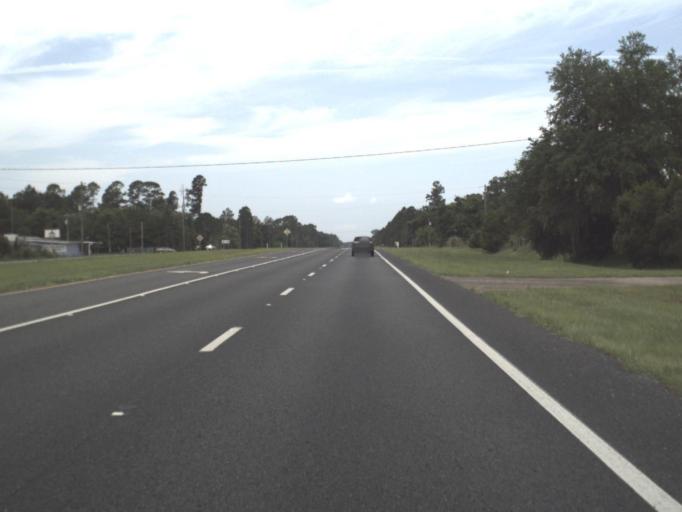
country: US
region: Florida
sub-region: Alachua County
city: Hawthorne
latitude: 29.5974
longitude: -82.1062
